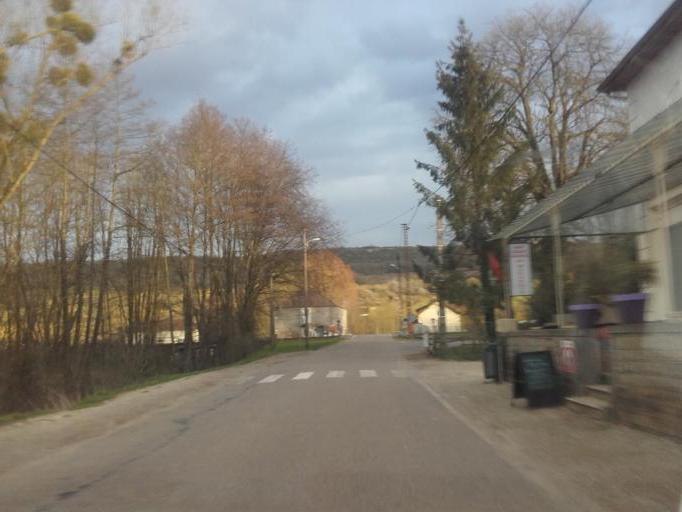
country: FR
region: Bourgogne
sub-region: Departement de Saone-et-Loire
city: Saint-Leger-sur-Dheune
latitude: 46.8935
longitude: 4.6757
